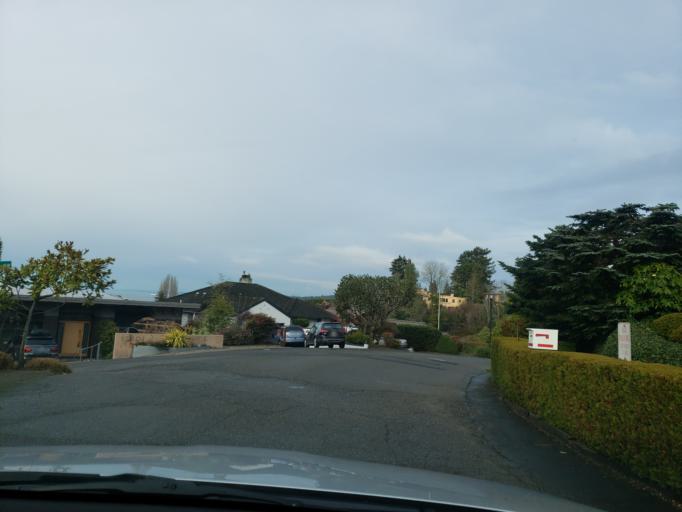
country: US
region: Washington
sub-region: King County
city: Shoreline
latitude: 47.7022
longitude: -122.3821
